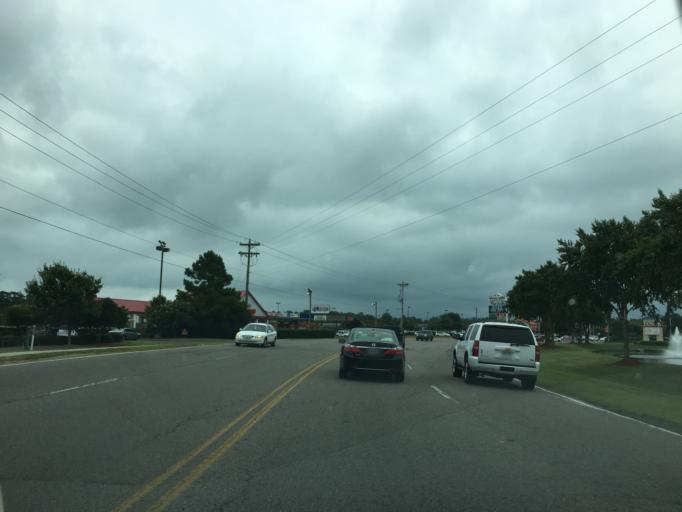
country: US
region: South Carolina
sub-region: Horry County
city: North Myrtle Beach
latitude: 33.7862
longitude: -78.7716
